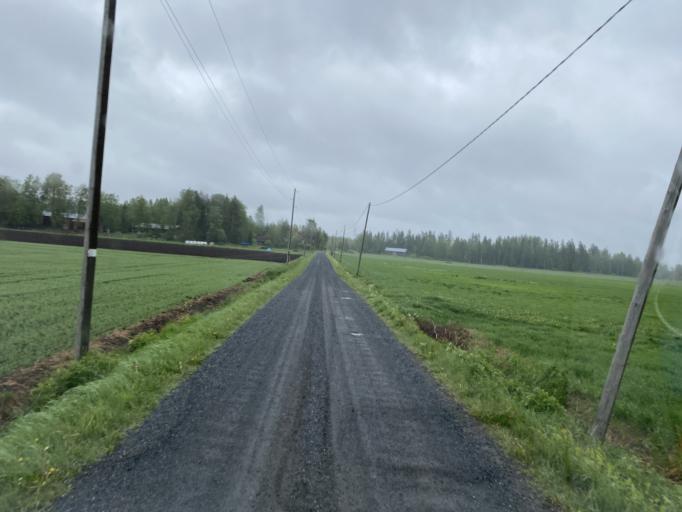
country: FI
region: Pirkanmaa
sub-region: Etelae-Pirkanmaa
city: Urjala
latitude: 60.9498
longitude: 23.5486
